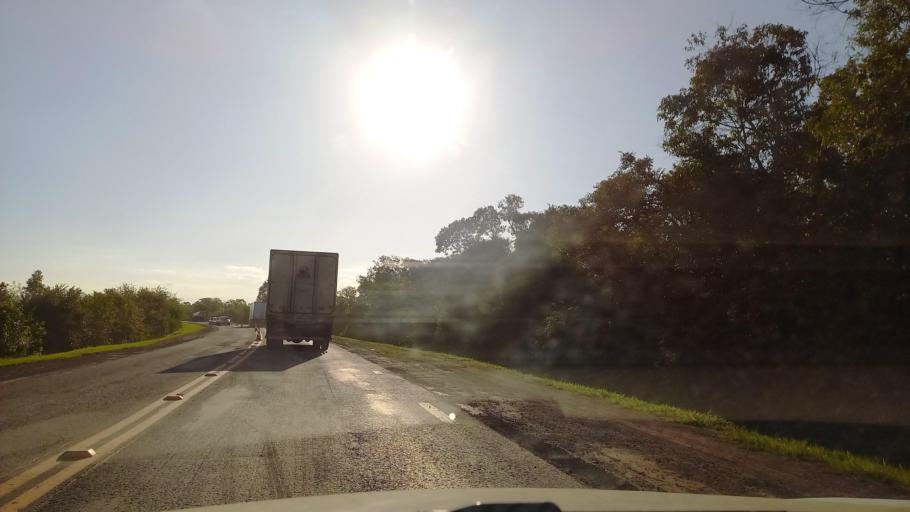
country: BR
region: Rio Grande do Sul
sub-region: Taquari
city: Taquari
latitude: -29.6879
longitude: -51.9531
